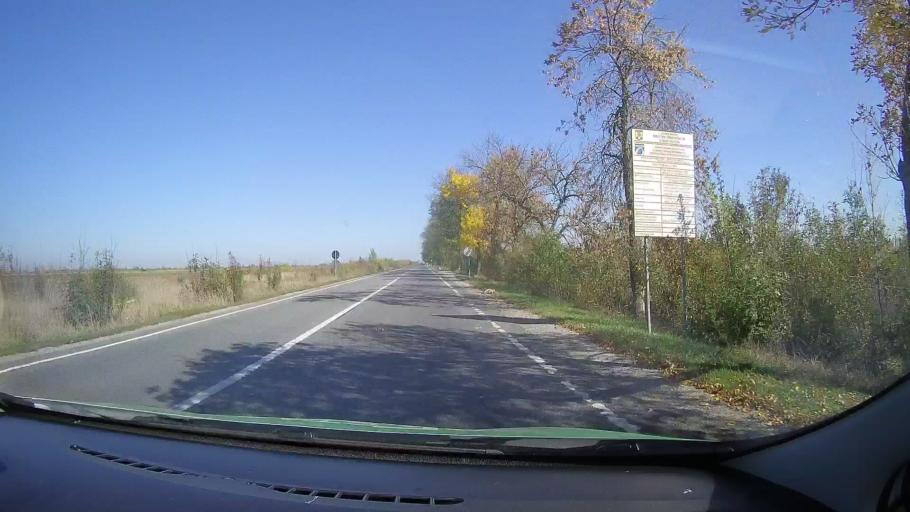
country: RO
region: Satu Mare
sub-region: Comuna Moftinu
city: Moftinu Mic
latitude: 47.6999
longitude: 22.6264
